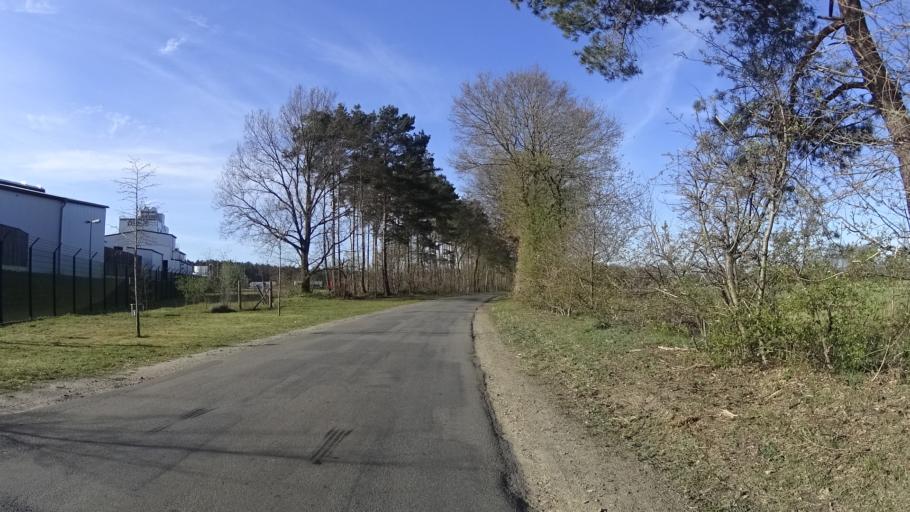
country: DE
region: Lower Saxony
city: Haren
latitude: 52.7712
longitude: 7.2731
